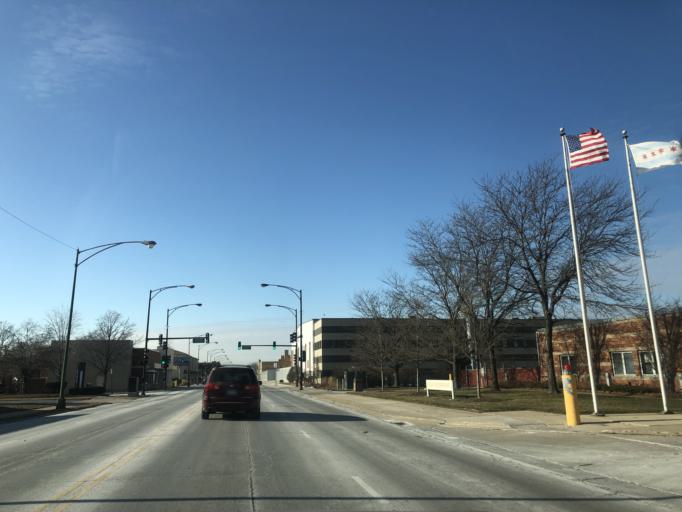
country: US
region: Illinois
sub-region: Cook County
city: Hometown
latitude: 41.7782
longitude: -87.7524
